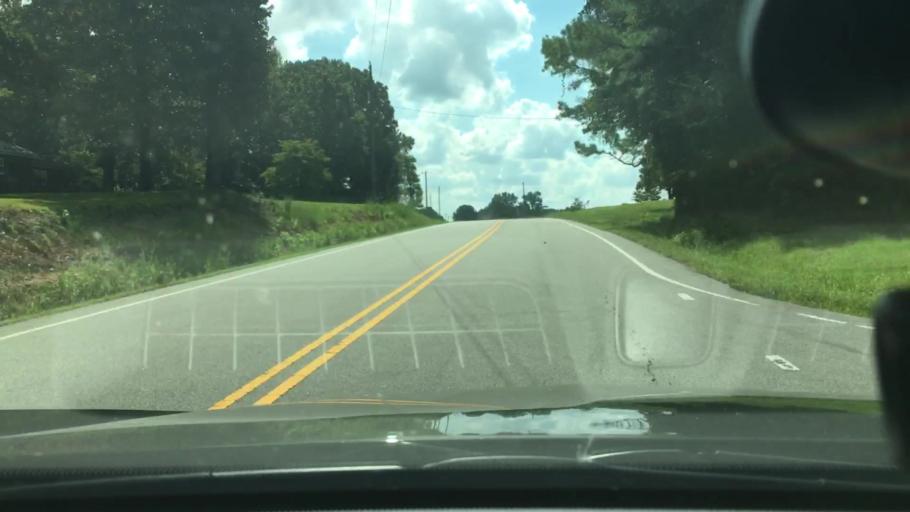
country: US
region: North Carolina
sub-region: Edgecombe County
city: Pinetops
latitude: 35.7196
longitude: -77.5288
